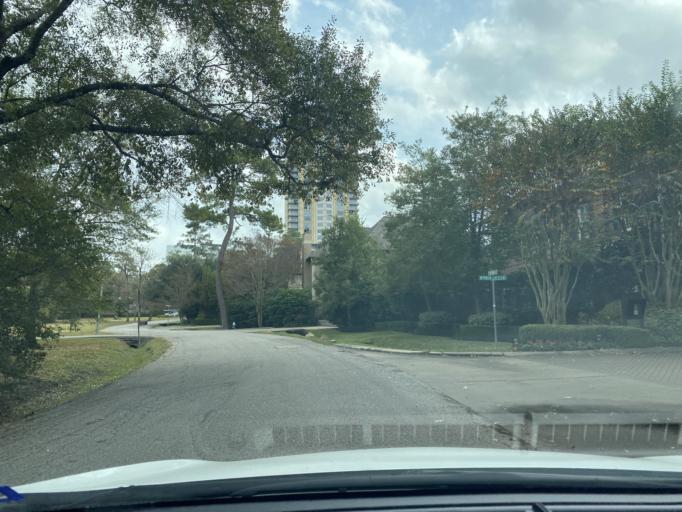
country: US
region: Texas
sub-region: Harris County
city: Hunters Creek Village
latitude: 29.7567
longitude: -95.4612
